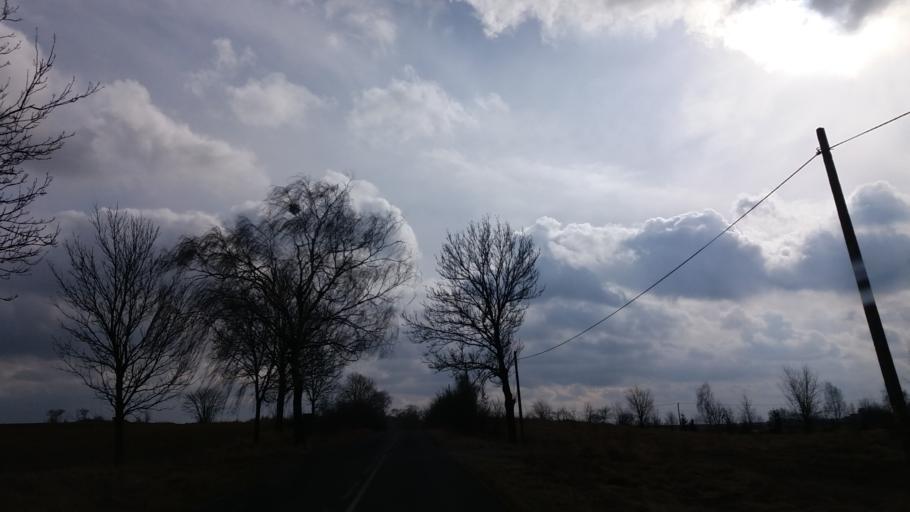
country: PL
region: West Pomeranian Voivodeship
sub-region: Powiat choszczenski
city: Drawno
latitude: 53.2417
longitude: 15.7343
